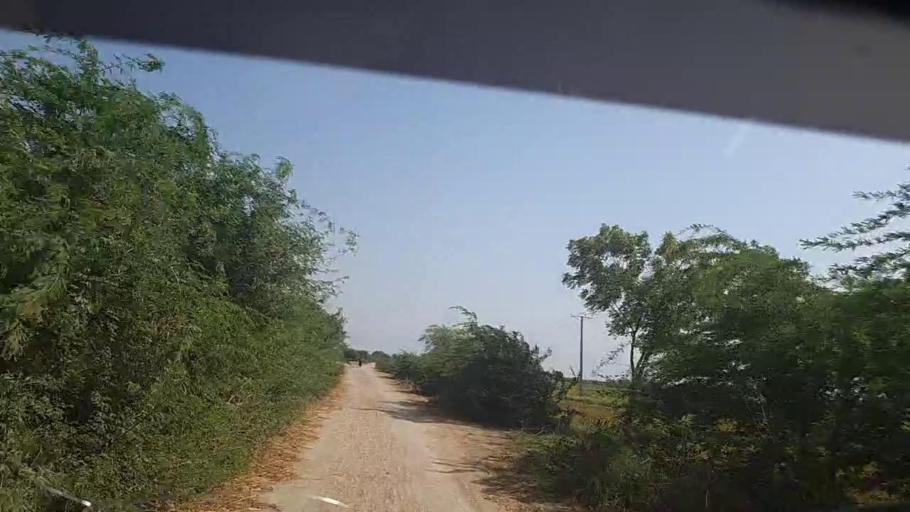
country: PK
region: Sindh
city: Rajo Khanani
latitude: 24.9597
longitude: 68.8932
